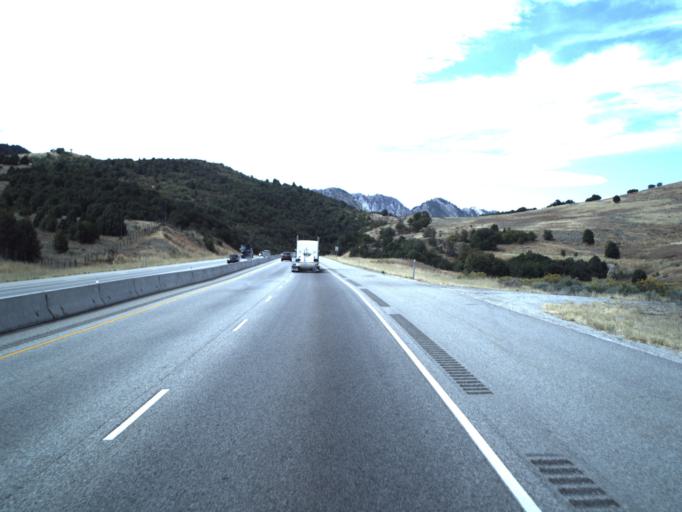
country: US
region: Utah
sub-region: Box Elder County
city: Brigham City
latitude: 41.5279
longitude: -111.9510
